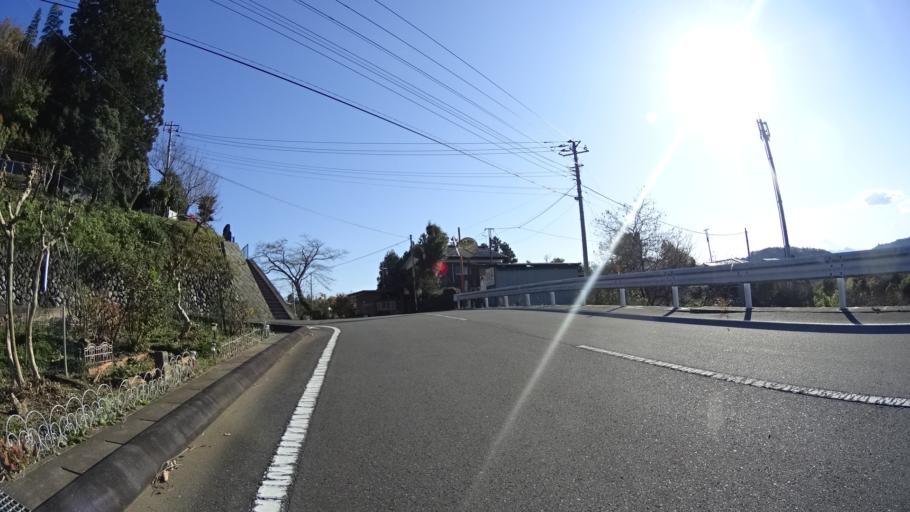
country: JP
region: Yamanashi
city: Uenohara
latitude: 35.6630
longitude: 139.1161
